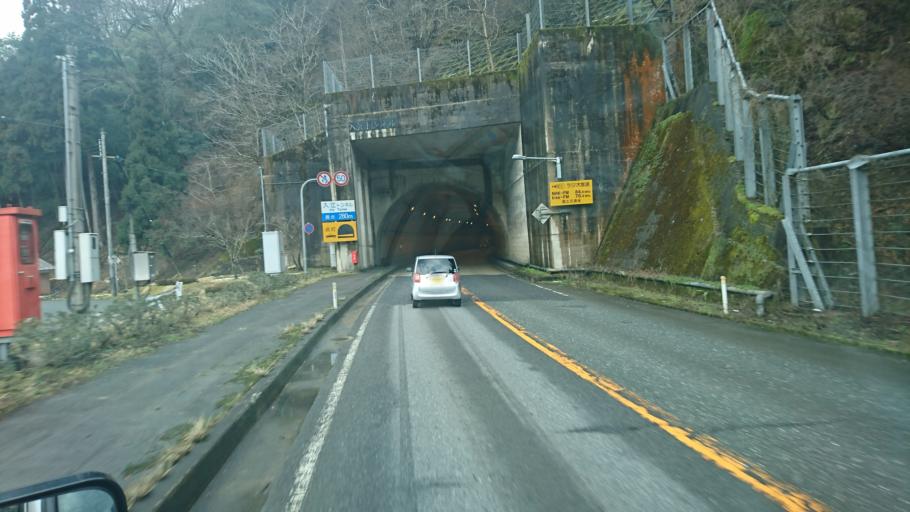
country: JP
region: Hyogo
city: Toyooka
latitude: 35.4937
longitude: 134.5657
